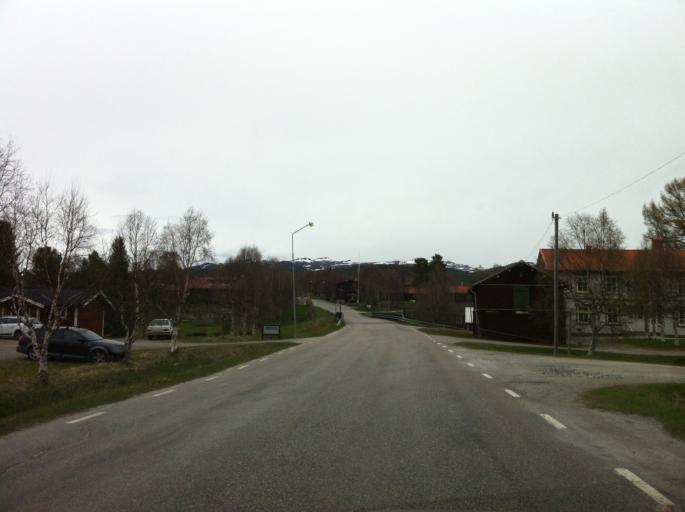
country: NO
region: Hedmark
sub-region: Engerdal
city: Engerdal
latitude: 62.5257
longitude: 12.5930
